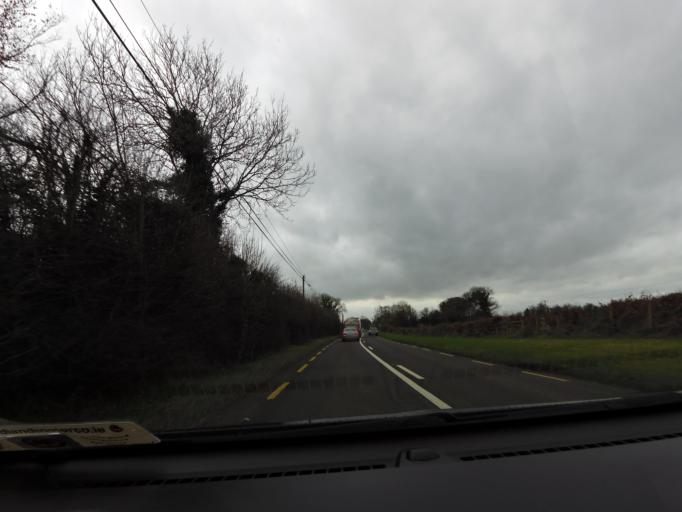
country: IE
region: Leinster
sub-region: Kilkenny
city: Ballyragget
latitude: 52.7357
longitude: -7.3178
